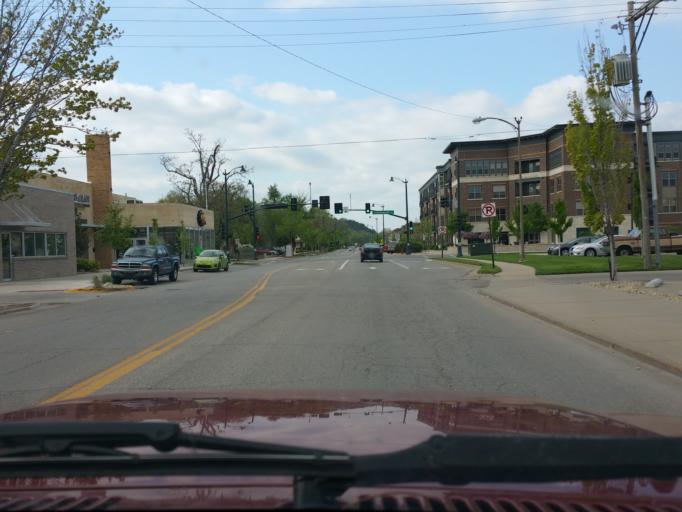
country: US
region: Kansas
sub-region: Riley County
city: Manhattan
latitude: 39.1807
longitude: -96.5618
